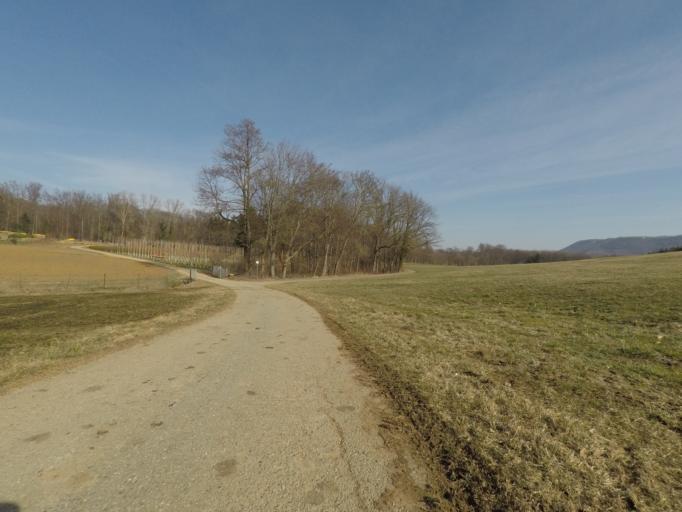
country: DE
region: Baden-Wuerttemberg
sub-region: Tuebingen Region
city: Eningen unter Achalm
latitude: 48.5043
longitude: 9.2728
